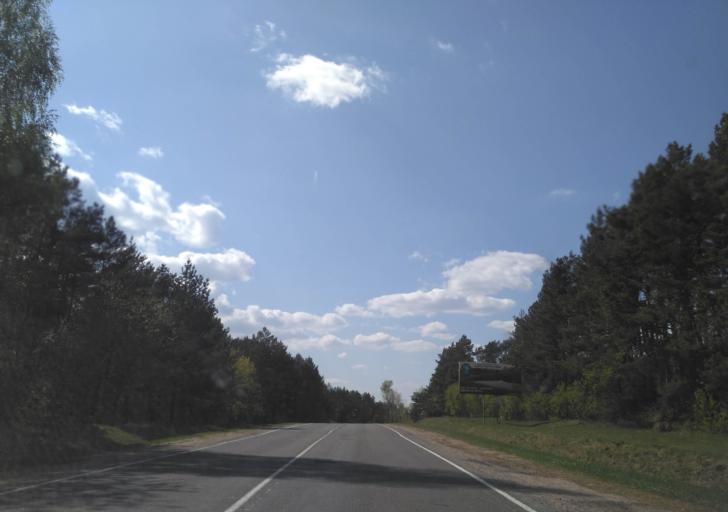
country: BY
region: Minsk
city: Narach
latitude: 54.8862
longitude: 26.8002
